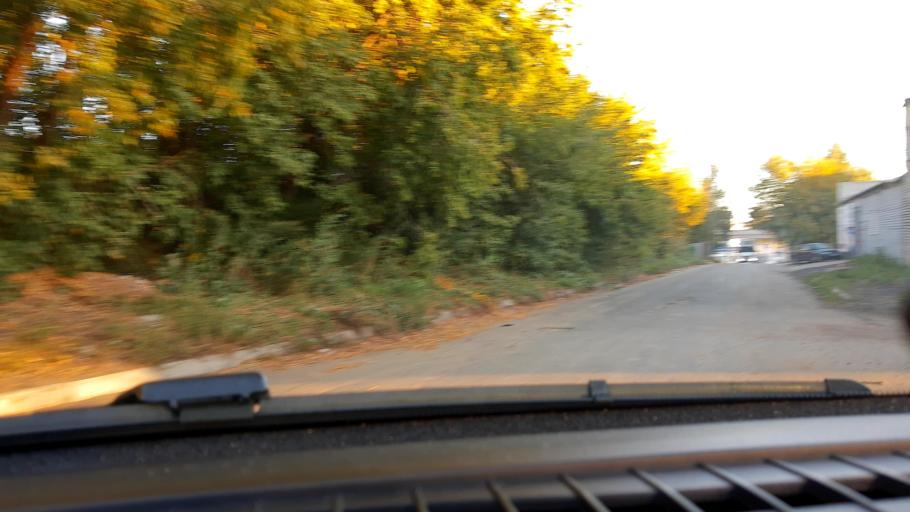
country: RU
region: Nizjnij Novgorod
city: Nizhniy Novgorod
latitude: 56.2370
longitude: 44.0001
